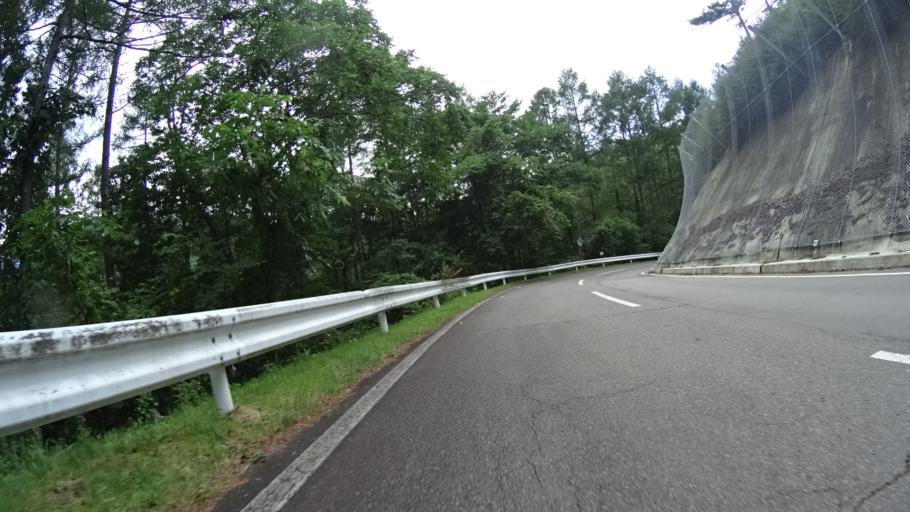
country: JP
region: Nagano
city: Saku
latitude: 36.0700
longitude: 138.6321
